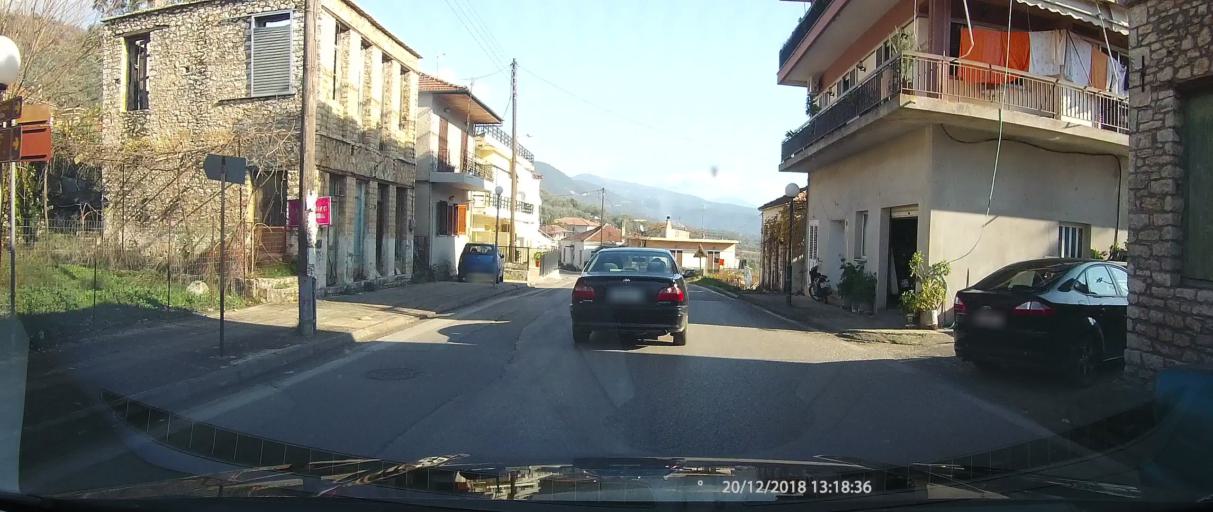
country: GR
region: West Greece
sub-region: Nomos Aitolias kai Akarnanias
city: Paravola
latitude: 38.6138
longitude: 21.5238
